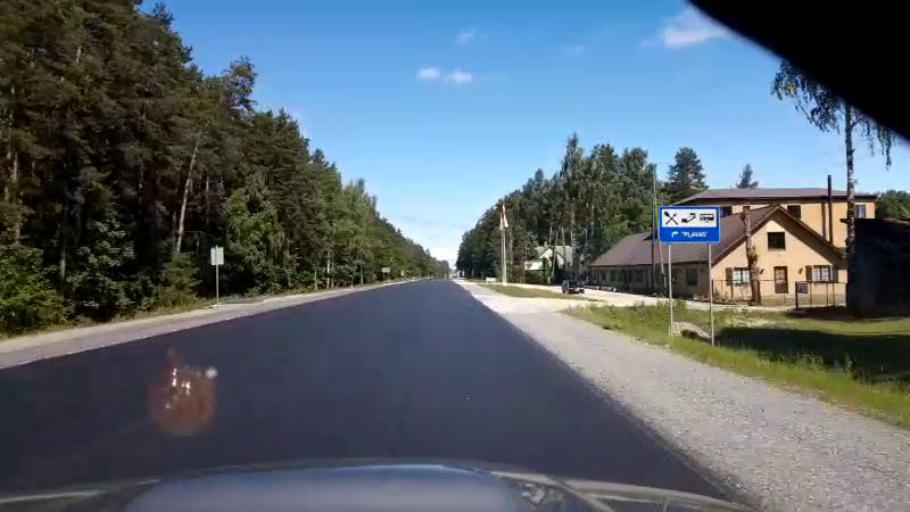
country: LV
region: Salacgrivas
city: Ainazi
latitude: 57.8444
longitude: 24.3503
